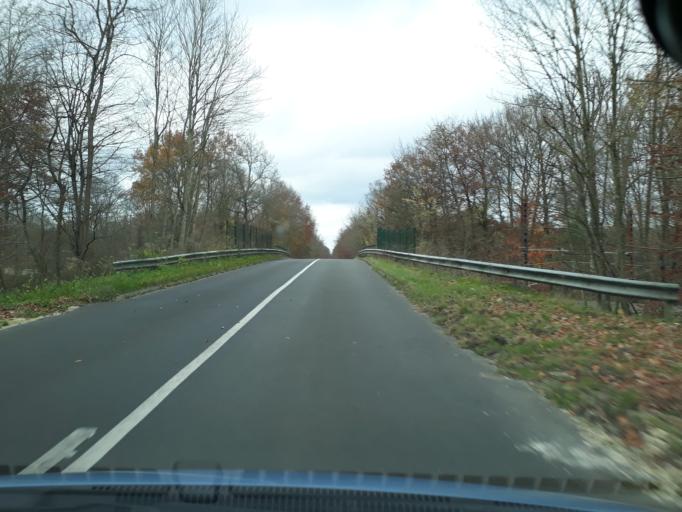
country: FR
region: Ile-de-France
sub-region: Departement de Seine-et-Marne
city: Thomery
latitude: 48.3935
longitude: 2.7695
